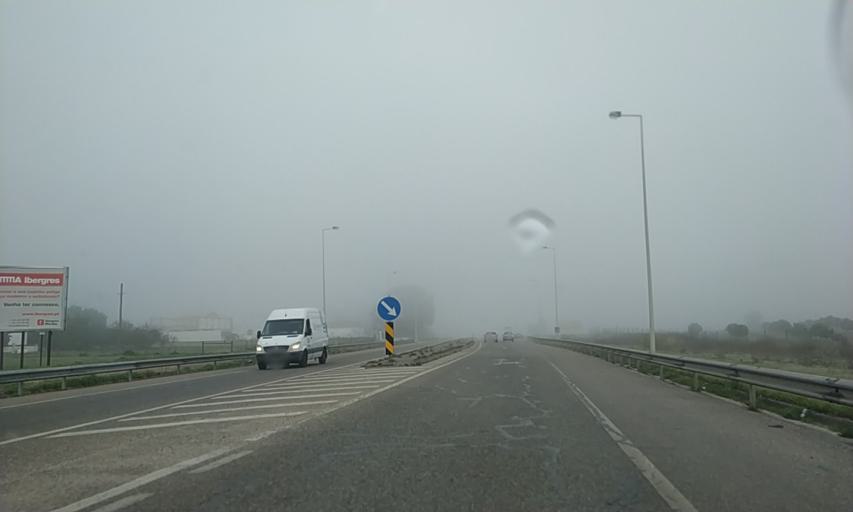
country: PT
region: Setubal
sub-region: Palmela
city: Pinhal Novo
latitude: 38.6486
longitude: -8.9157
